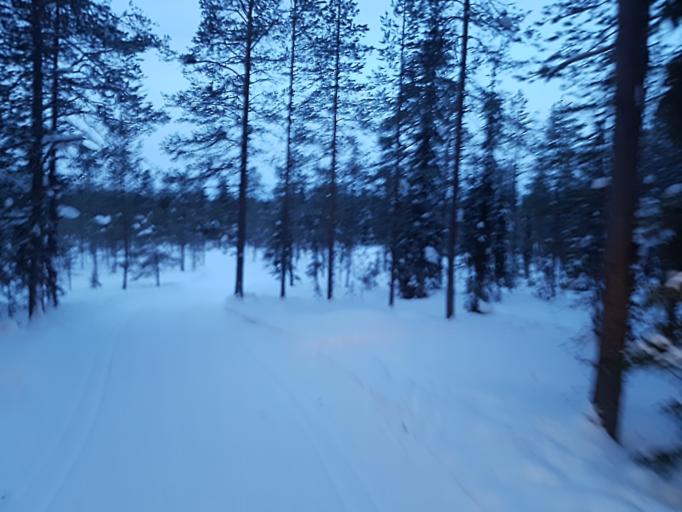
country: FI
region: Lapland
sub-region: Tunturi-Lappi
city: Kolari
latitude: 67.6222
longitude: 24.1445
